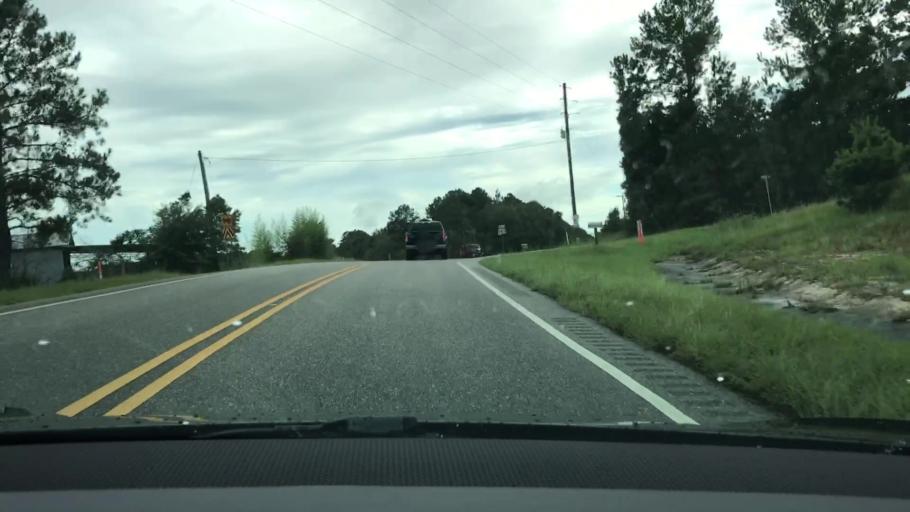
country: US
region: Alabama
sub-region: Geneva County
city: Samson
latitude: 31.0410
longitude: -86.1017
